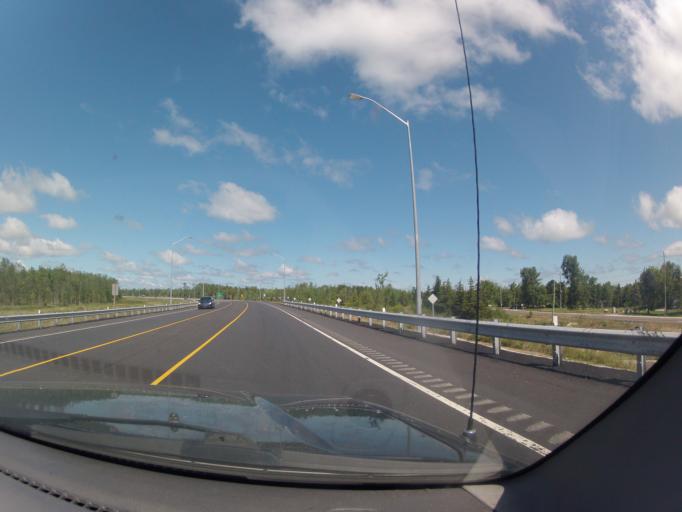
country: CA
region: Ontario
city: Wasaga Beach
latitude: 44.4582
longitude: -80.1055
